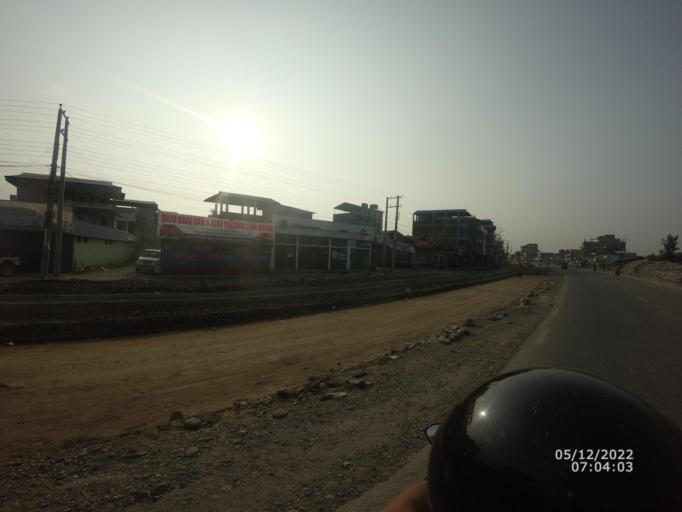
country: NP
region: Central Region
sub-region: Narayani Zone
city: Bharatpur
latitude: 27.6736
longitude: 84.4322
